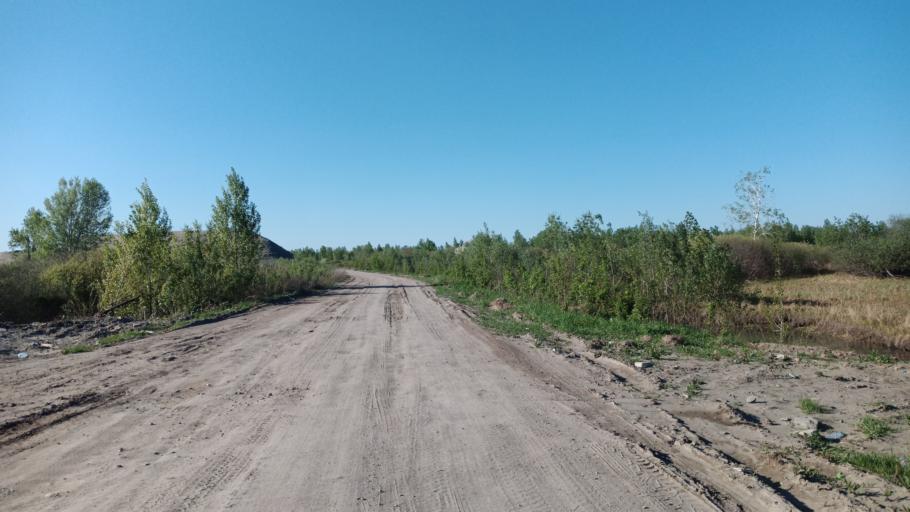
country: RU
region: Altai Krai
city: Zaton
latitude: 53.3082
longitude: 83.8238
